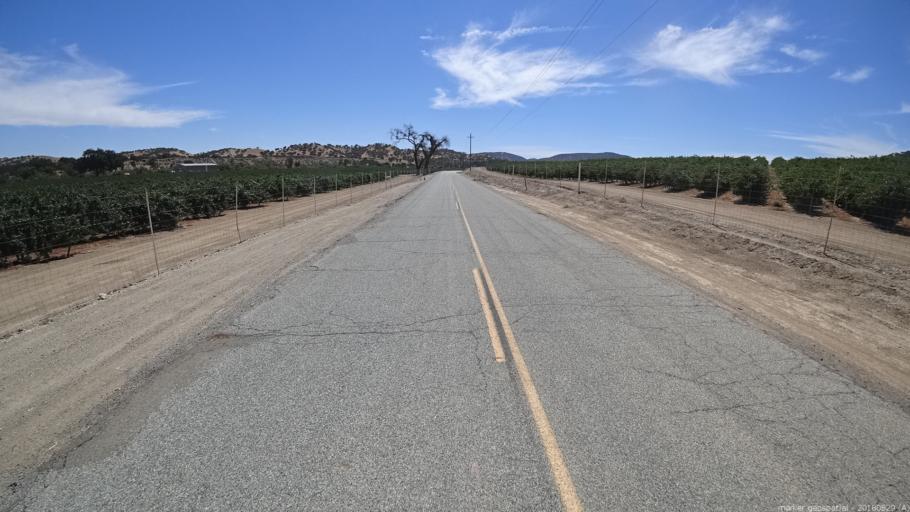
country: US
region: California
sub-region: San Luis Obispo County
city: Lake Nacimiento
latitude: 35.8167
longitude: -120.8448
